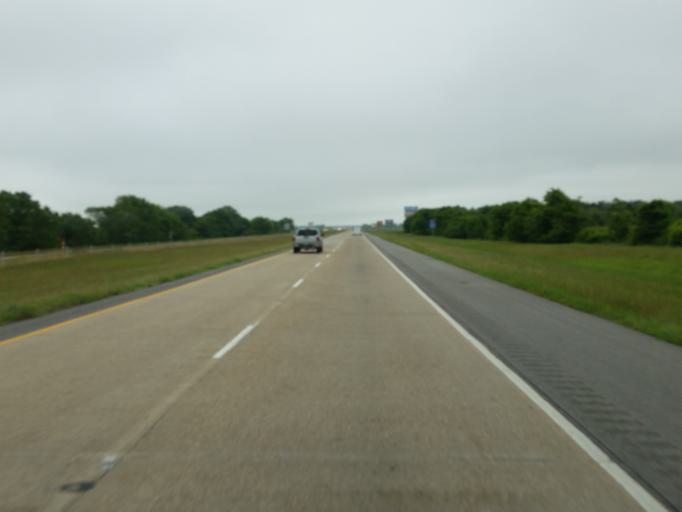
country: US
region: Mississippi
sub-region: Warren County
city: Vicksburg
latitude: 32.3284
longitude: -91.0162
